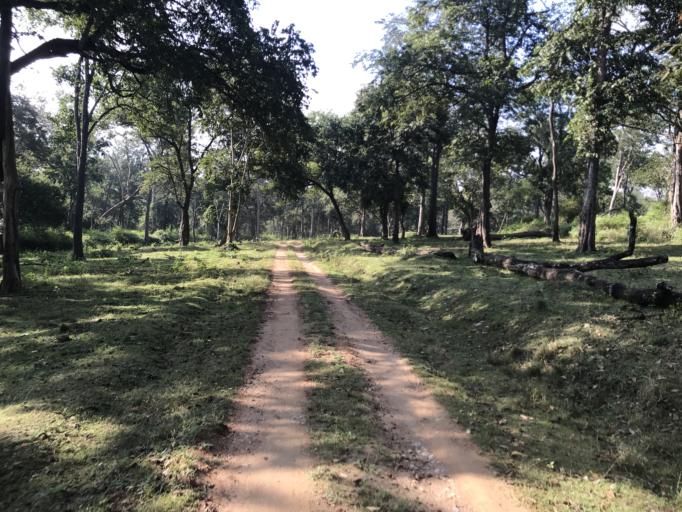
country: IN
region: Karnataka
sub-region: Mysore
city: Heggadadevankote
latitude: 11.9473
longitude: 76.2188
